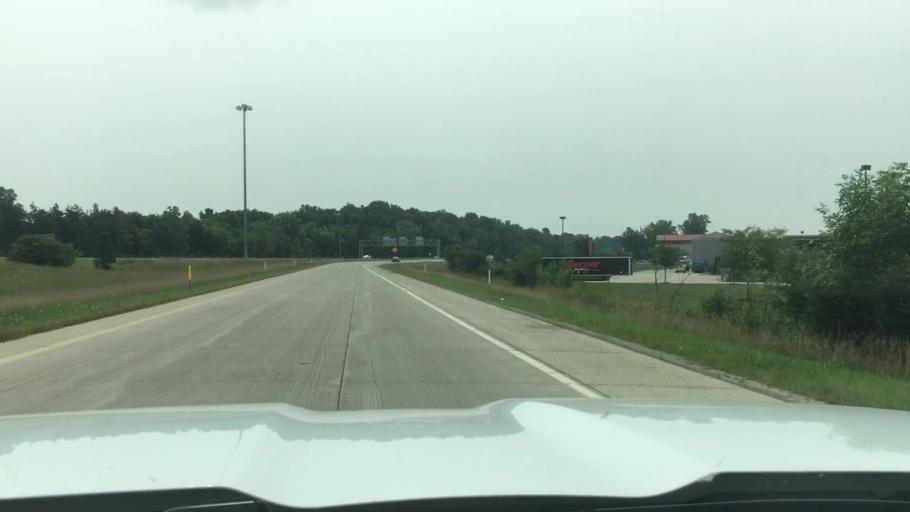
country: US
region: Michigan
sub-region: Eaton County
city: Waverly
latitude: 42.7392
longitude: -84.6698
